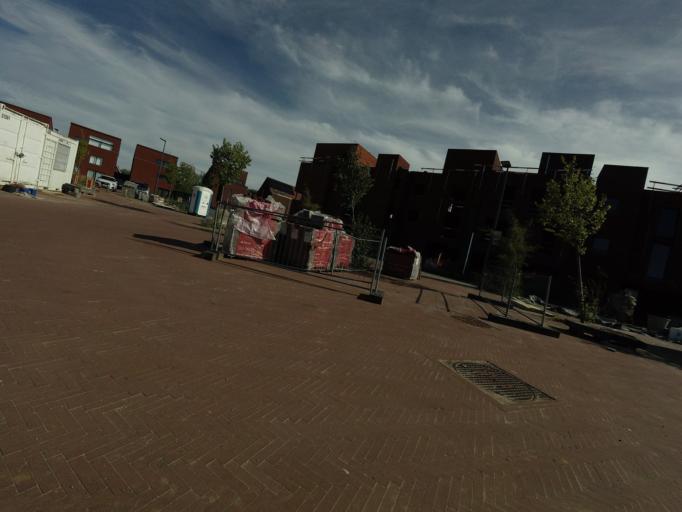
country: BE
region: Flanders
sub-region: Provincie Vlaams-Brabant
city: Herent
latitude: 50.9010
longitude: 4.6718
